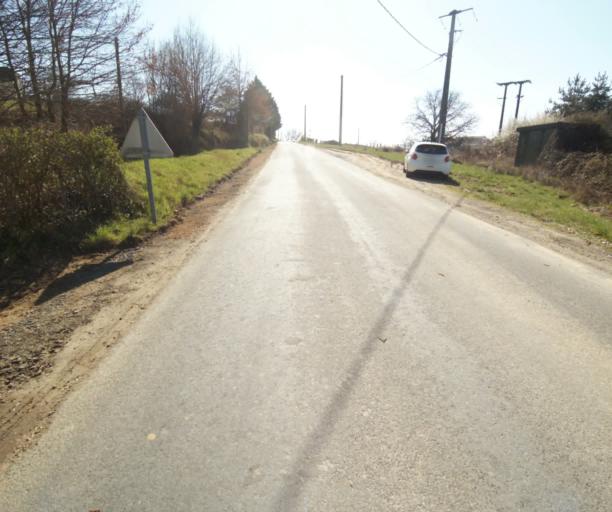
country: FR
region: Limousin
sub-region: Departement de la Correze
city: Saint-Mexant
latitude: 45.2825
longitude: 1.6200
